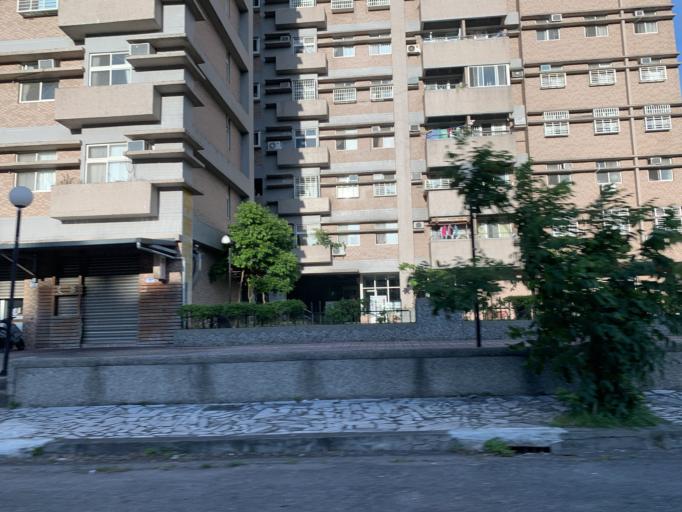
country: TW
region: Taiwan
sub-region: Hualien
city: Hualian
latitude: 24.0038
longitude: 121.6294
